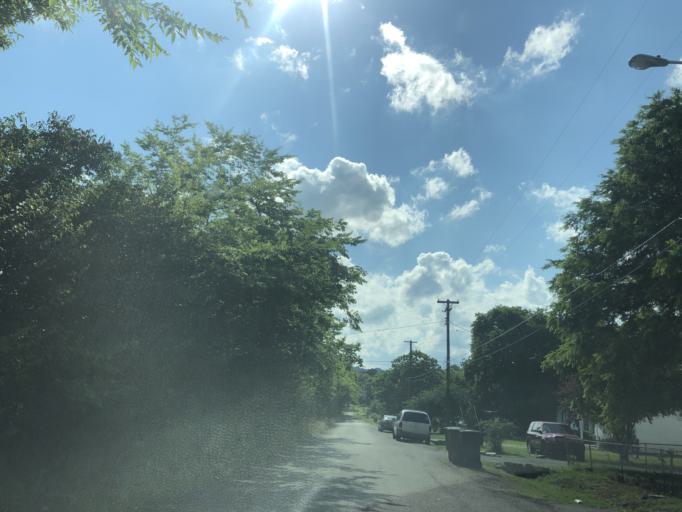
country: US
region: Tennessee
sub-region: Davidson County
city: Nashville
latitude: 36.2379
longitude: -86.8194
